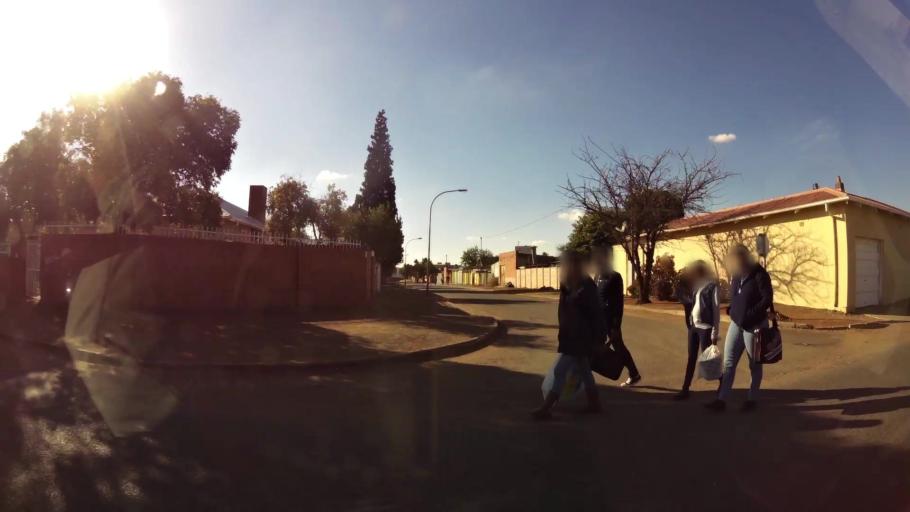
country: ZA
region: Northern Cape
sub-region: Frances Baard District Municipality
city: Kimberley
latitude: -28.7483
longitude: 24.7612
